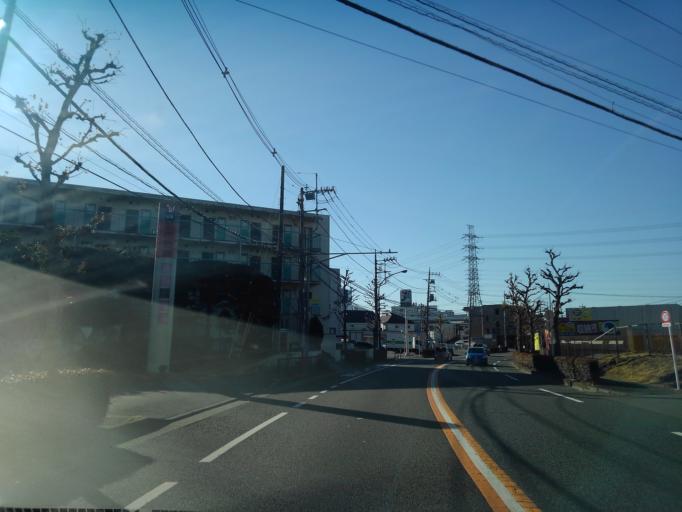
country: JP
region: Tokyo
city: Hino
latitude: 35.6748
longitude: 139.3643
